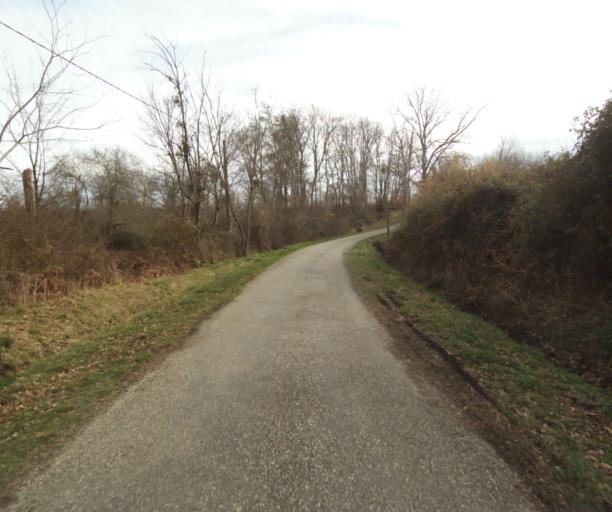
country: FR
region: Aquitaine
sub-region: Departement des Landes
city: Gabarret
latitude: 43.9677
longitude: 0.0379
